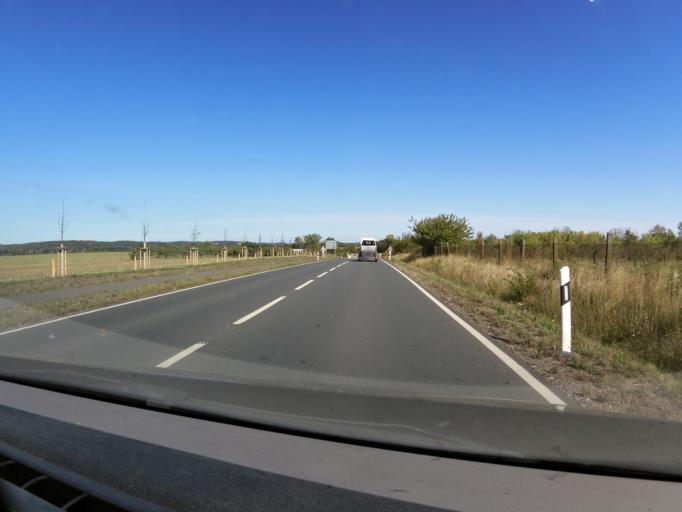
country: DE
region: Saxony-Anhalt
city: Bad Suderode
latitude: 51.7496
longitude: 11.1246
